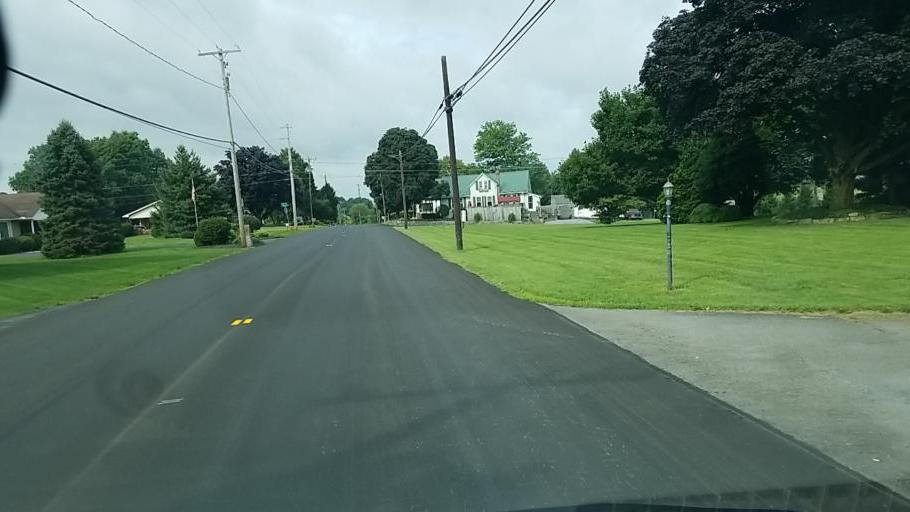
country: US
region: Pennsylvania
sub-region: Dauphin County
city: Millersburg
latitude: 40.5529
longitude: -76.9380
